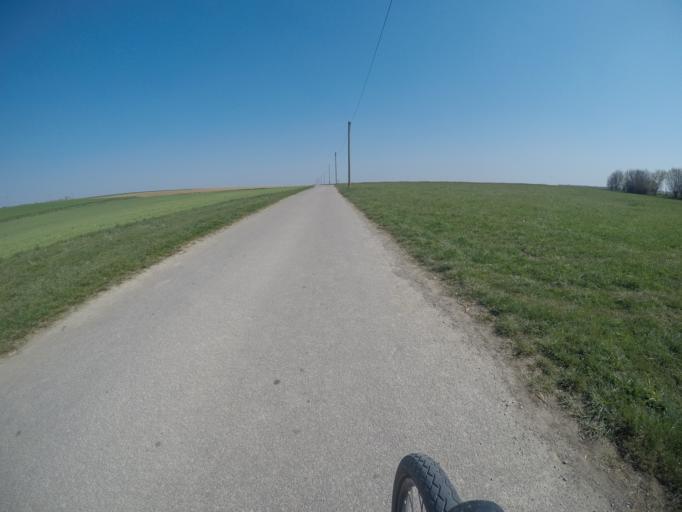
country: DE
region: Baden-Wuerttemberg
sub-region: Regierungsbezirk Stuttgart
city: Weil der Stadt
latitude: 48.7323
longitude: 8.9058
